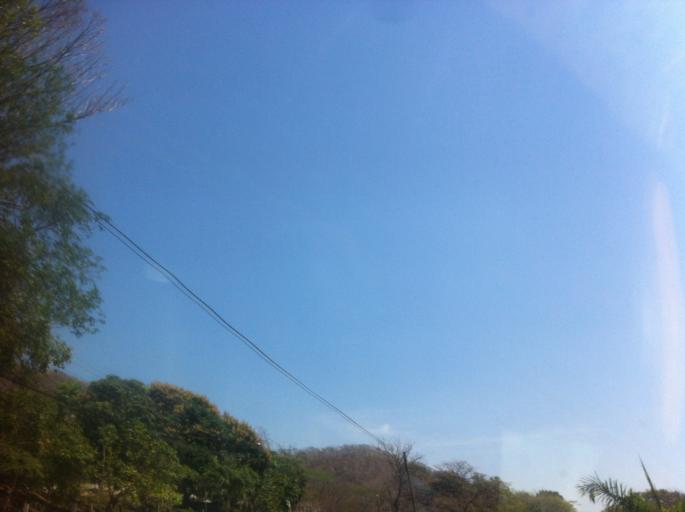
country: CR
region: Guanacaste
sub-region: Canton de Nicoya
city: Nicoya
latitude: 10.1202
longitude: -85.4472
